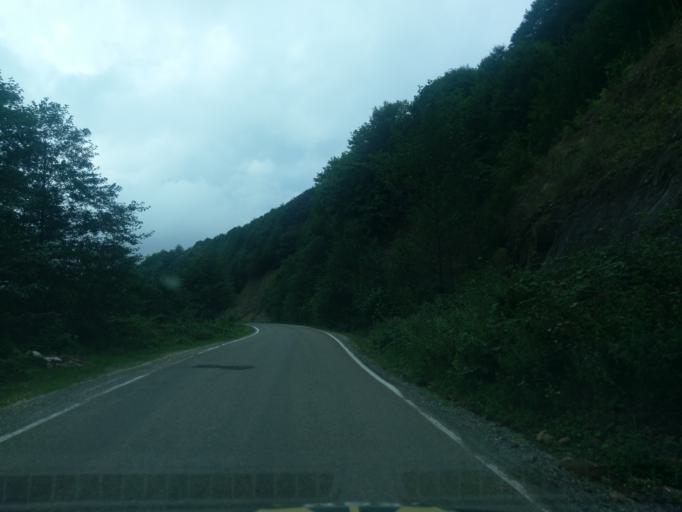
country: TR
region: Ordu
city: Gurgentepe
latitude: 40.8579
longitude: 37.6508
